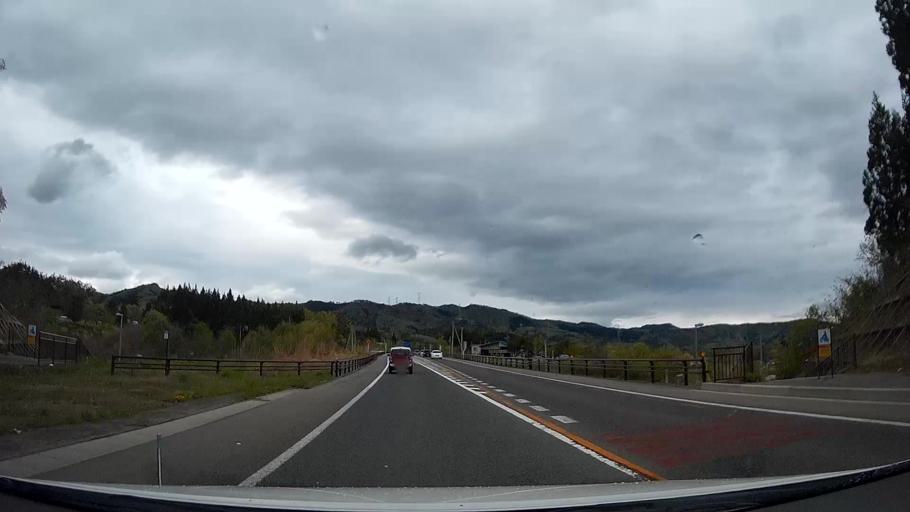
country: JP
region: Yamagata
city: Kaminoyama
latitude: 38.1115
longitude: 140.2112
